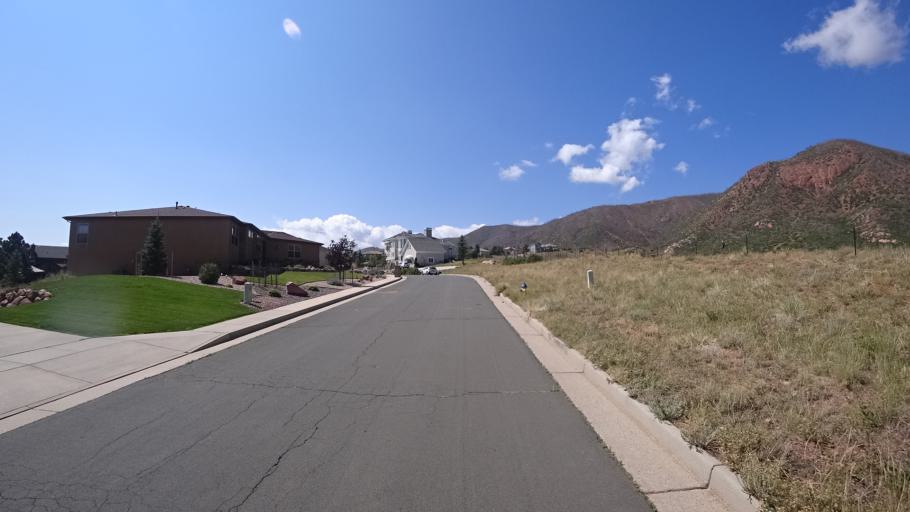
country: US
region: Colorado
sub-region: El Paso County
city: Air Force Academy
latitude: 38.9249
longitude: -104.8789
